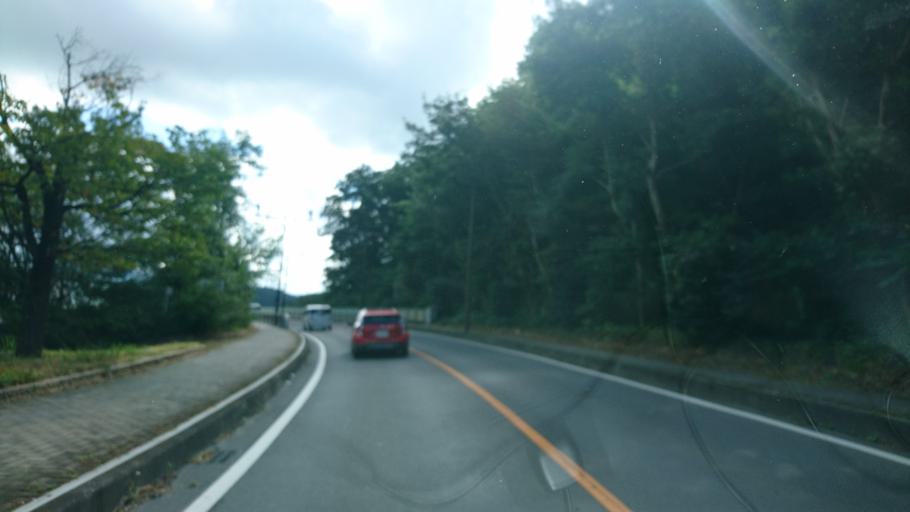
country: JP
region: Gunma
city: Kiryu
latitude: 36.4154
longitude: 139.3145
